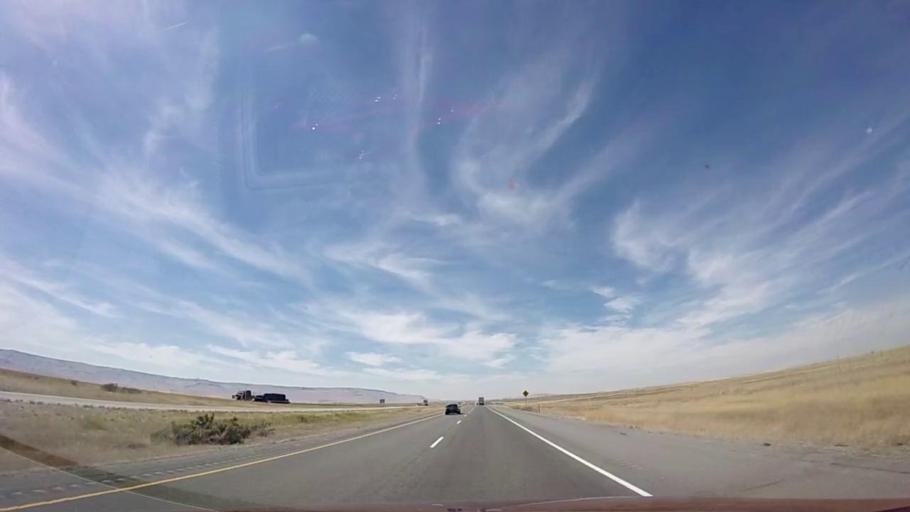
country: US
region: Idaho
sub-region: Minidoka County
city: Rupert
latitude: 42.4161
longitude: -113.3200
